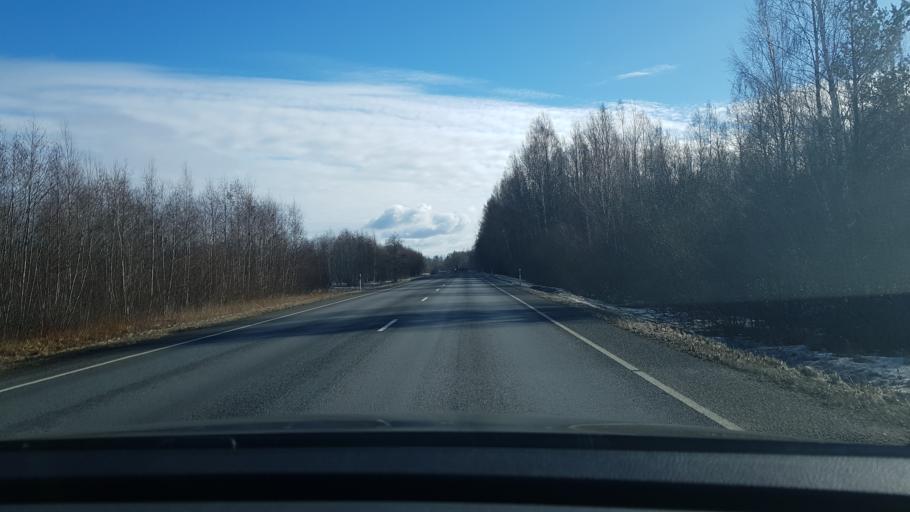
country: EE
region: Paernumaa
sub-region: Paikuse vald
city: Paikuse
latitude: 58.1964
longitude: 24.7467
